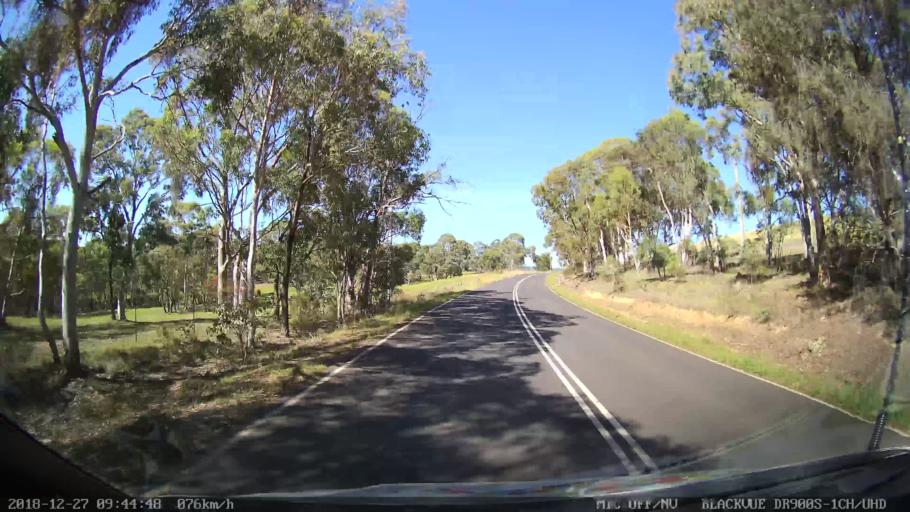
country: AU
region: New South Wales
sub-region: Lithgow
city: Portland
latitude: -33.3194
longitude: 149.9905
